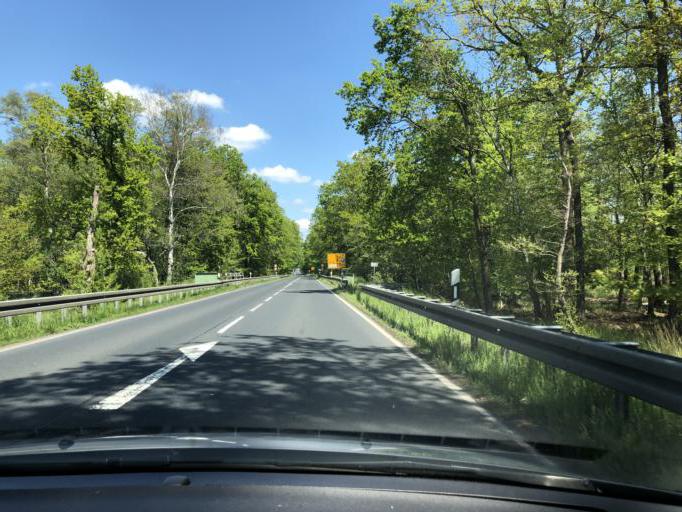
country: DE
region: Brandenburg
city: Herzberg
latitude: 51.6366
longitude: 13.1689
